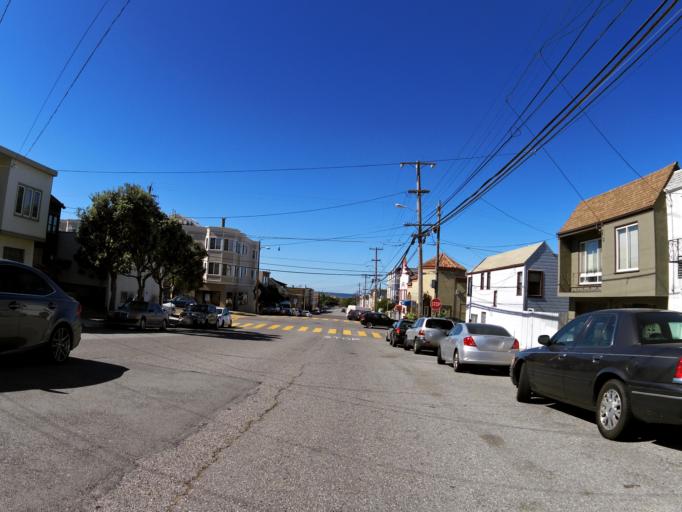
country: US
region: California
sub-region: San Mateo County
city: Daly City
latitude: 37.7624
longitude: -122.5055
